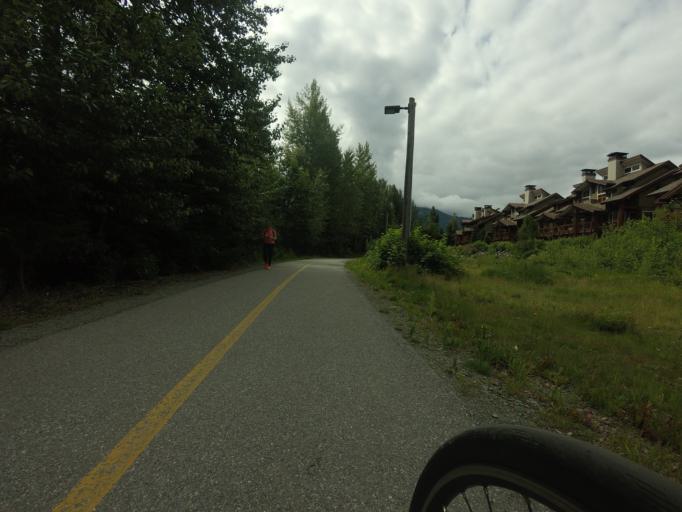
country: CA
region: British Columbia
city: Whistler
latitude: 50.1279
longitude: -122.9532
